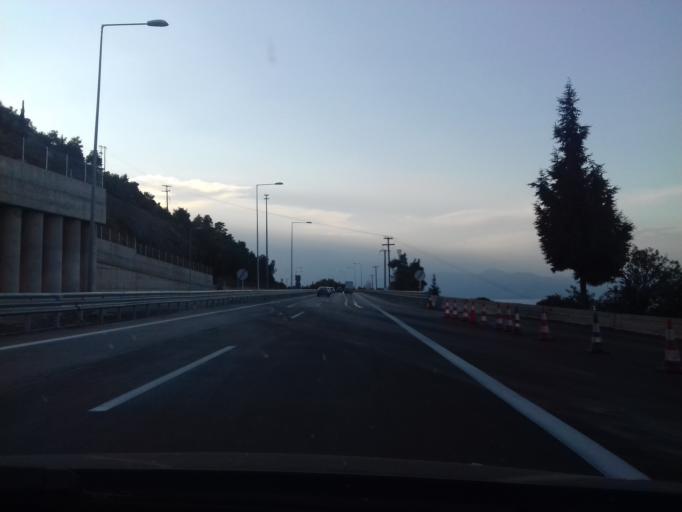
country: GR
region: West Greece
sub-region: Nomos Achaias
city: Akrata
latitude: 38.1696
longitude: 22.2619
